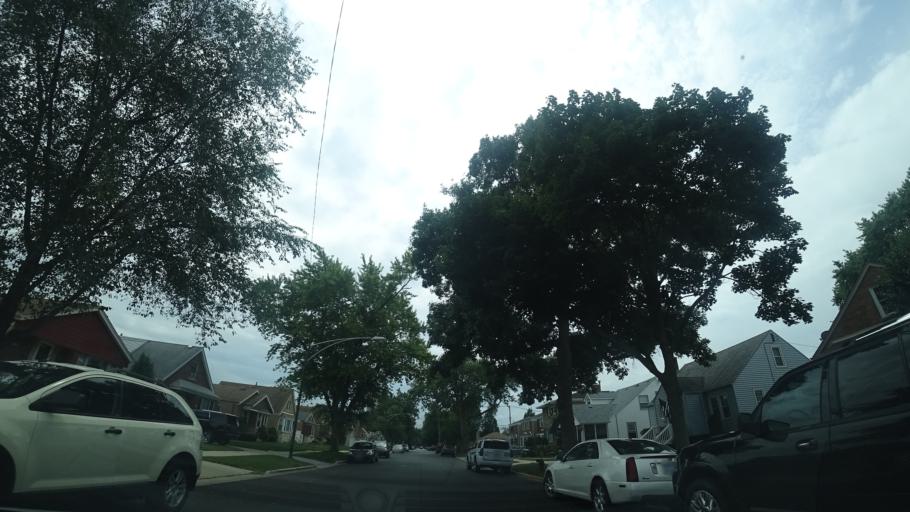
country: US
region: Illinois
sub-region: Cook County
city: Merrionette Park
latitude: 41.6999
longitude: -87.7133
